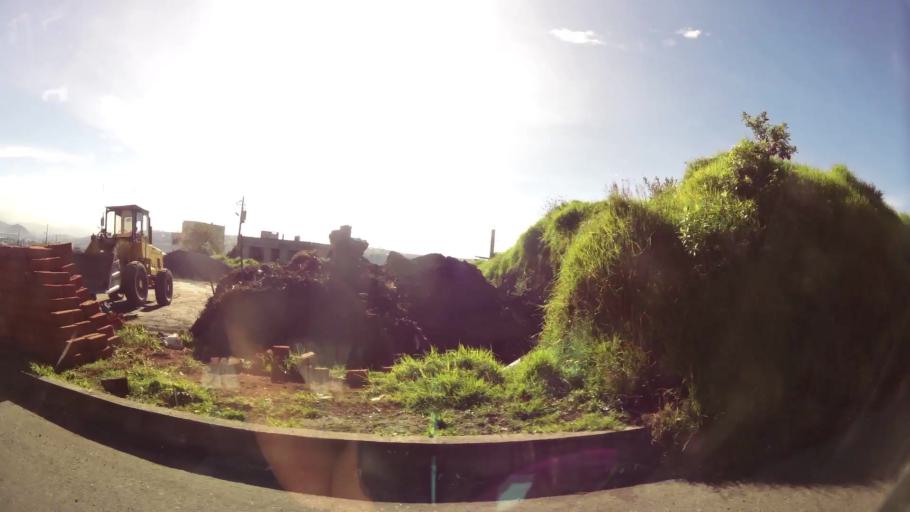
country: EC
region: Pichincha
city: Quito
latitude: -0.3221
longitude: -78.5567
